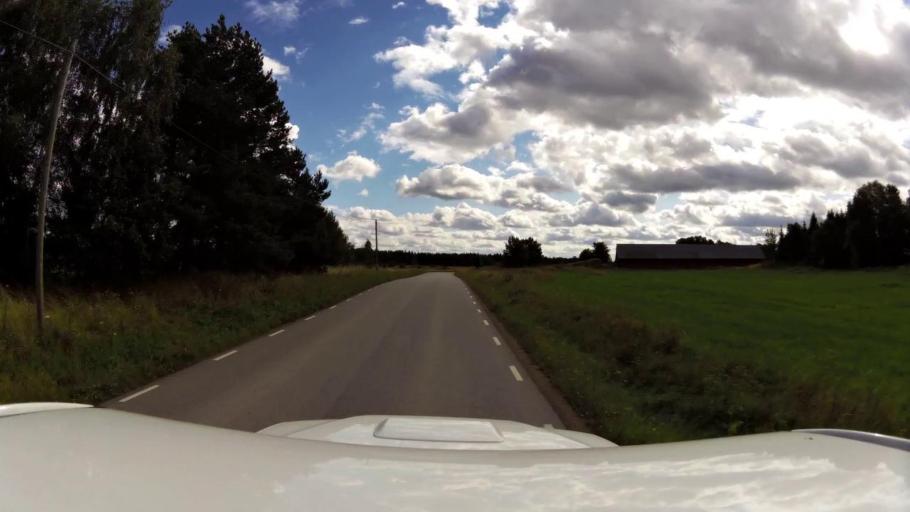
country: SE
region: OEstergoetland
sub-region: Linkopings Kommun
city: Linkoping
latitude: 58.3812
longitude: 15.5932
